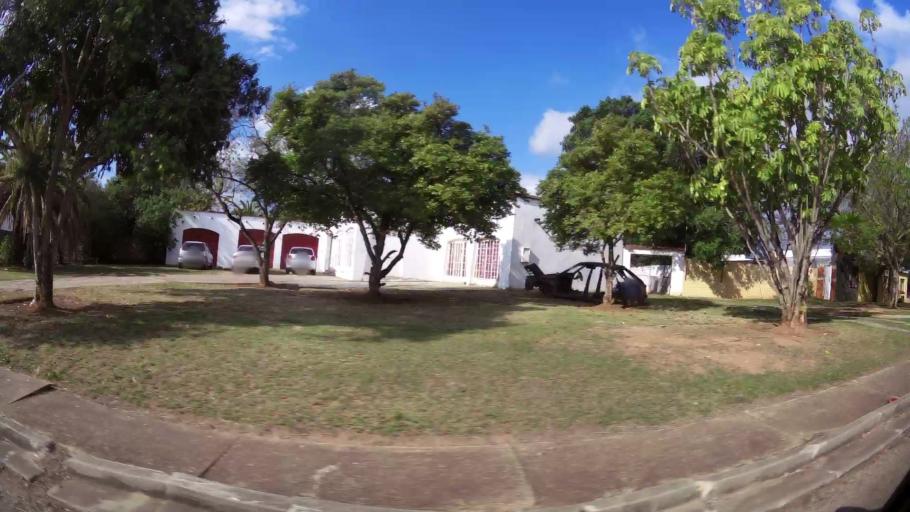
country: ZA
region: Eastern Cape
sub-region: Nelson Mandela Bay Metropolitan Municipality
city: Uitenhage
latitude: -33.7329
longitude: 25.4067
